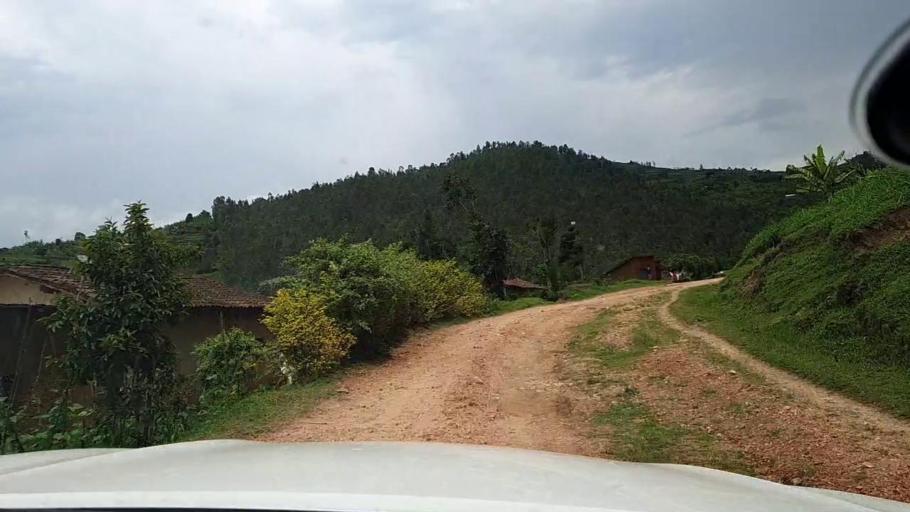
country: RW
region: Western Province
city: Kibuye
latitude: -2.0741
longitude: 29.4368
